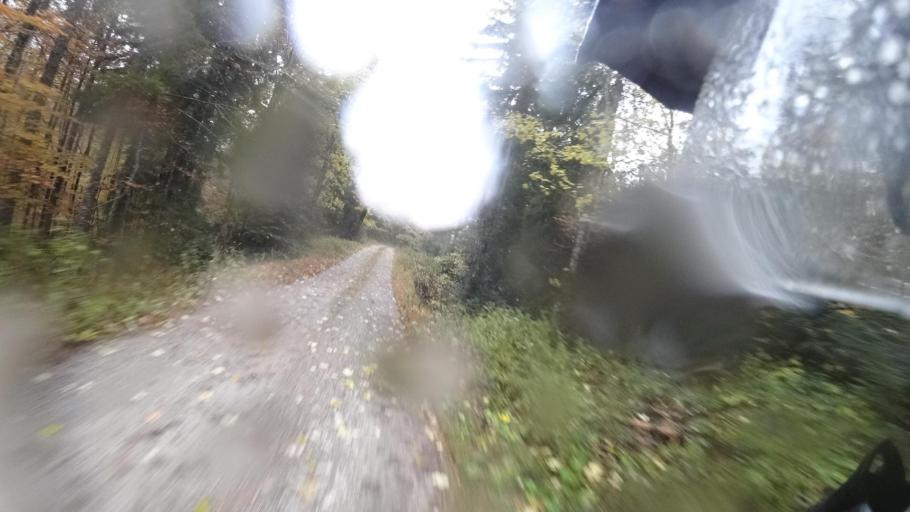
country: HR
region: Primorsko-Goranska
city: Vrbovsko
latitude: 45.3062
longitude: 14.9959
